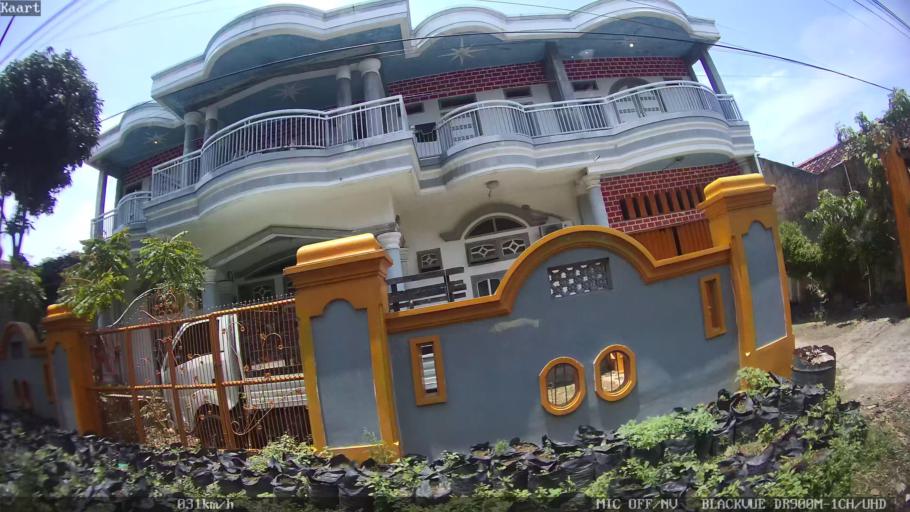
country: ID
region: Lampung
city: Kedaton
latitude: -5.3997
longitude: 105.2535
